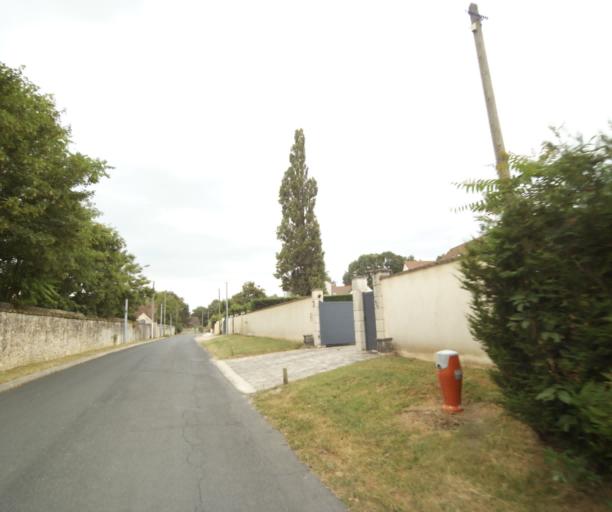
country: FR
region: Ile-de-France
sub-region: Departement de Seine-et-Marne
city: Cely
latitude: 48.4672
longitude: 2.5214
